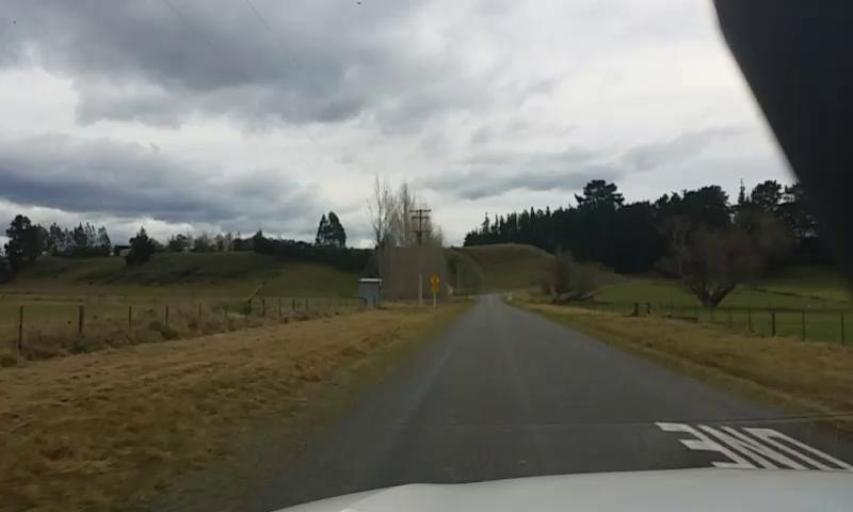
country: NZ
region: Canterbury
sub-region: Waimakariri District
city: Kaiapoi
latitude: -43.3005
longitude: 172.4378
